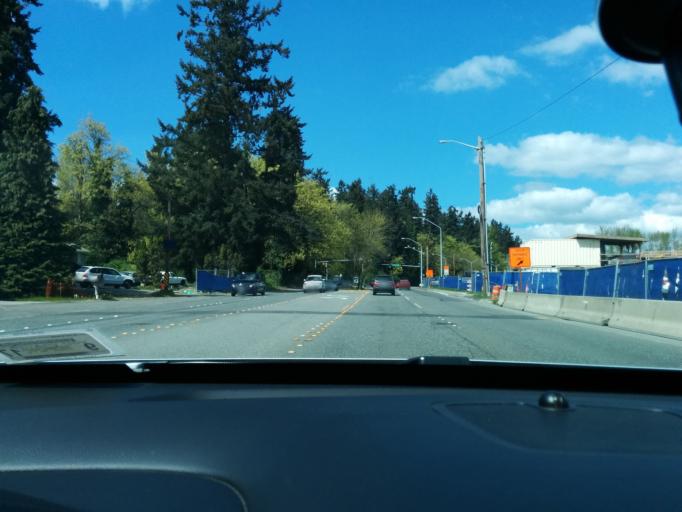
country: US
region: Washington
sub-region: King County
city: Newport
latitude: 47.5849
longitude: -122.1899
